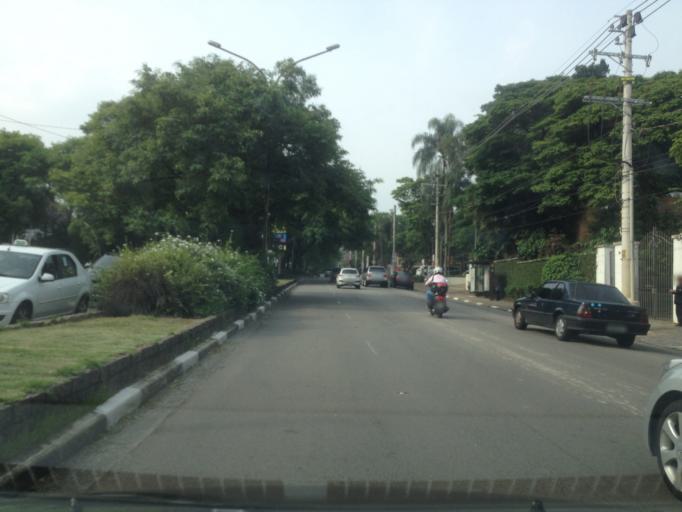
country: BR
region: Sao Paulo
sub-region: Sao Paulo
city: Sao Paulo
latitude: -23.5872
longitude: -46.6641
